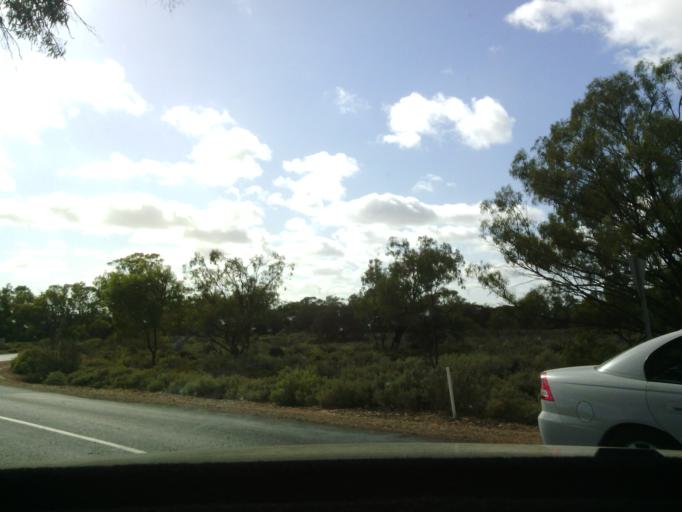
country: AU
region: South Australia
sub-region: Berri and Barmera
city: Berri
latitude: -34.2810
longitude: 140.6261
